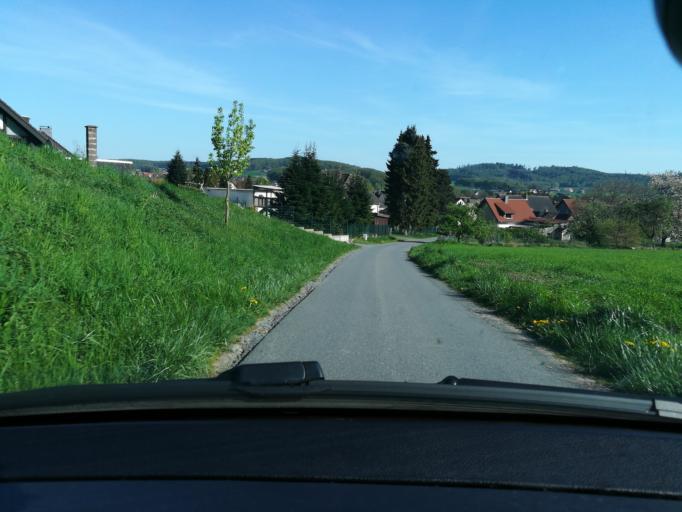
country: DE
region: North Rhine-Westphalia
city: Borgholzhausen
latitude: 52.1062
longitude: 8.2974
